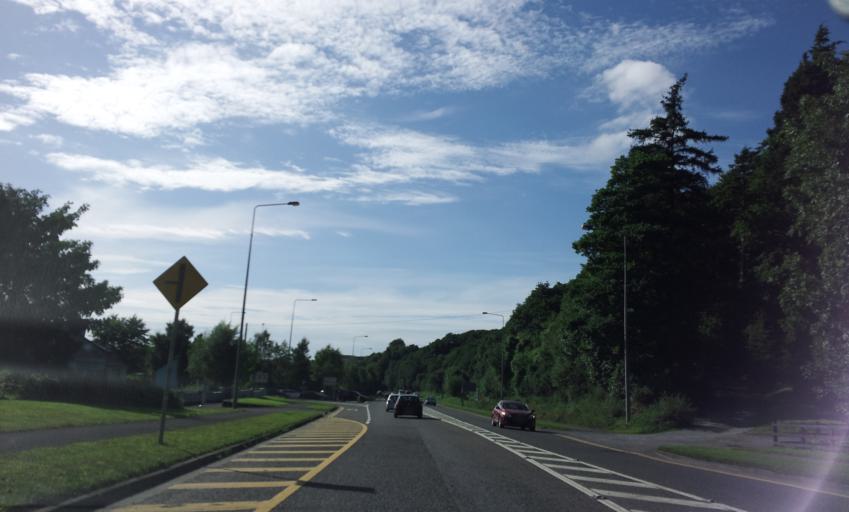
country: IE
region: Munster
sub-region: Ciarrai
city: Cill Airne
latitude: 52.0574
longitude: -9.4698
